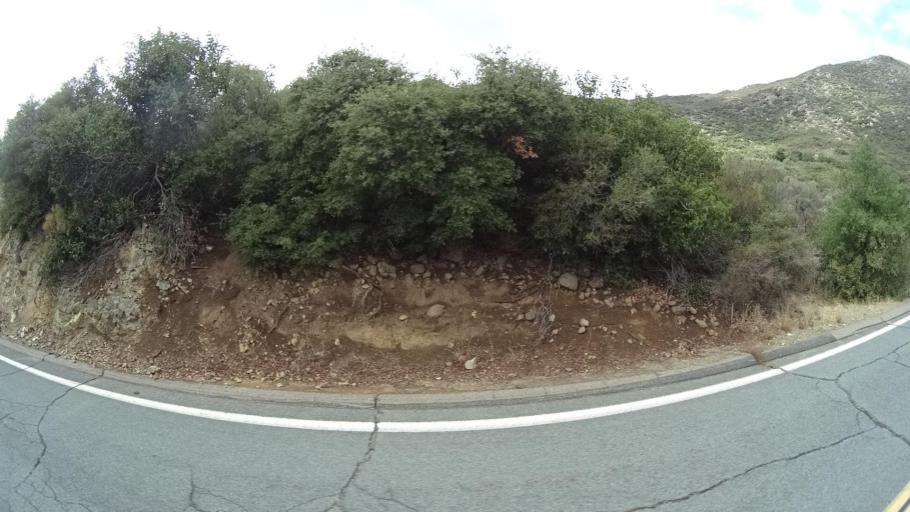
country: US
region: California
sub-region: San Diego County
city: Pine Valley
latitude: 32.7844
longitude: -116.4505
